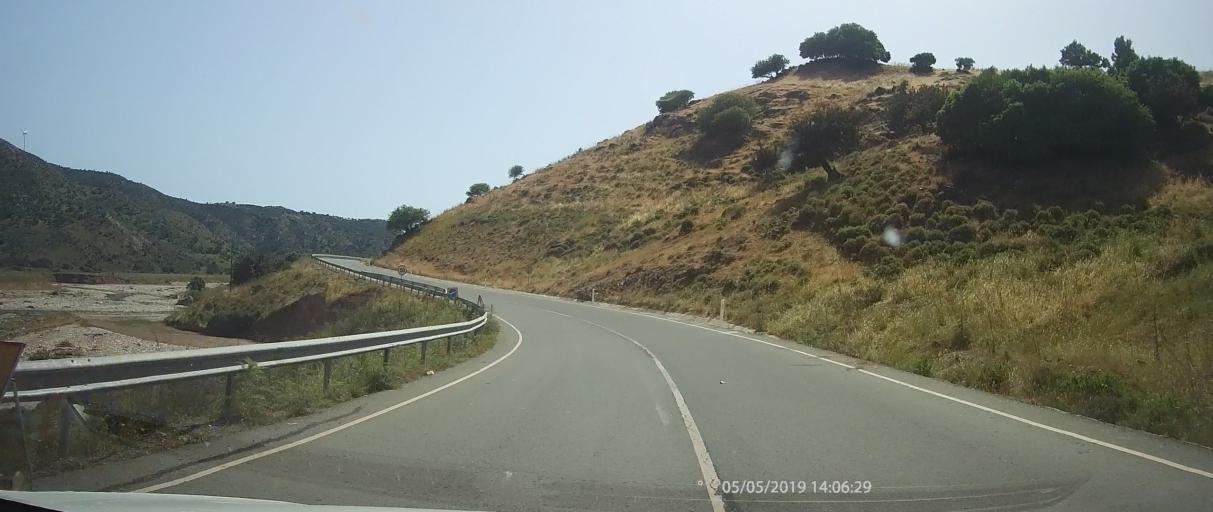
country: CY
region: Limassol
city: Pissouri
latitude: 34.7437
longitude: 32.6060
